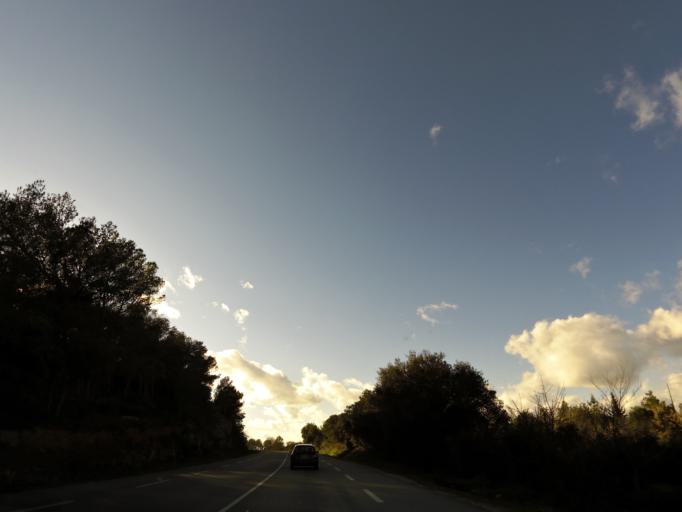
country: FR
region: Languedoc-Roussillon
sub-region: Departement du Gard
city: Caveirac
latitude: 43.8219
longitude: 4.2845
